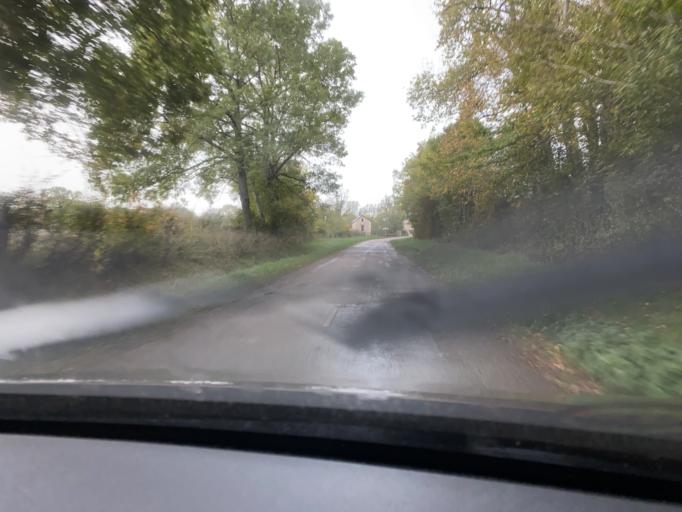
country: FR
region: Bourgogne
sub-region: Departement de la Cote-d'Or
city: Saulieu
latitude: 47.3595
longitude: 4.2546
